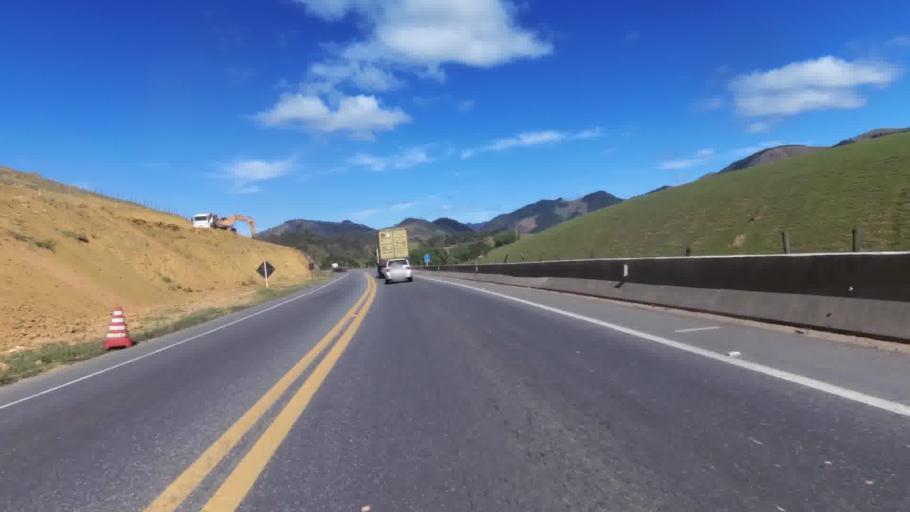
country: BR
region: Espirito Santo
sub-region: Iconha
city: Iconha
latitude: -20.7351
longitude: -40.7584
